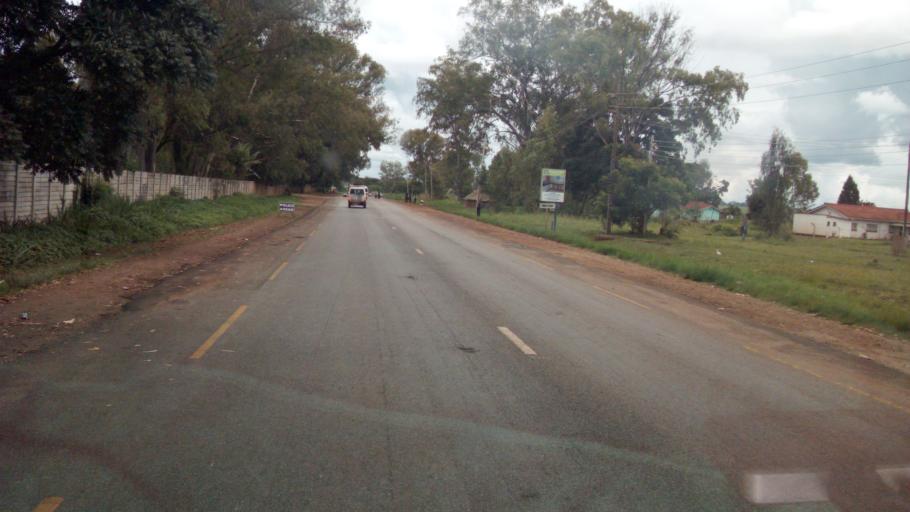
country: ZW
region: Harare
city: Harare
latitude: -17.7495
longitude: 31.0279
